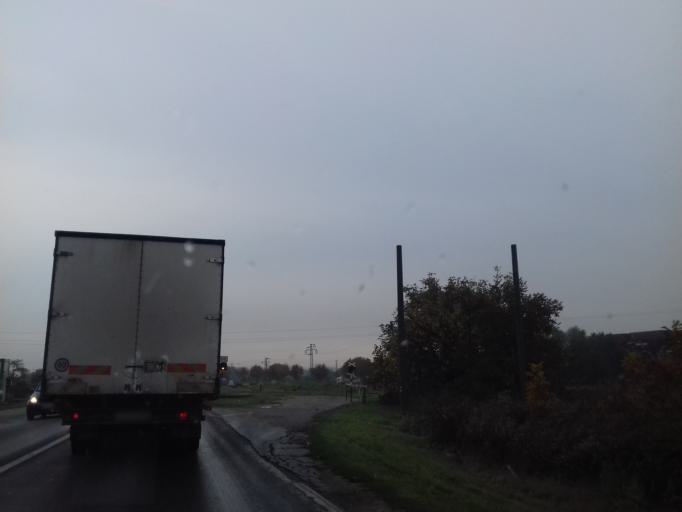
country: SK
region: Bratislavsky
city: Bratislava
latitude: 48.1346
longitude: 17.1644
